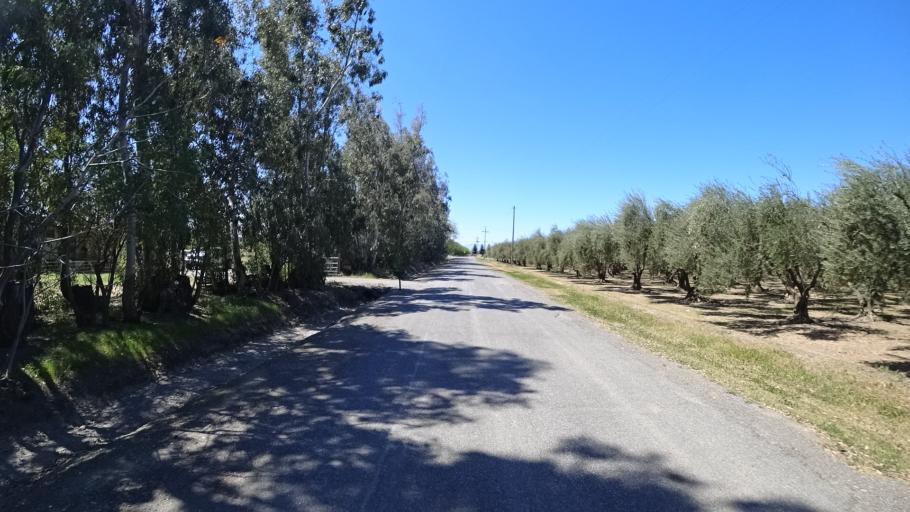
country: US
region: California
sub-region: Glenn County
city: Hamilton City
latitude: 39.7285
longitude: -122.1027
